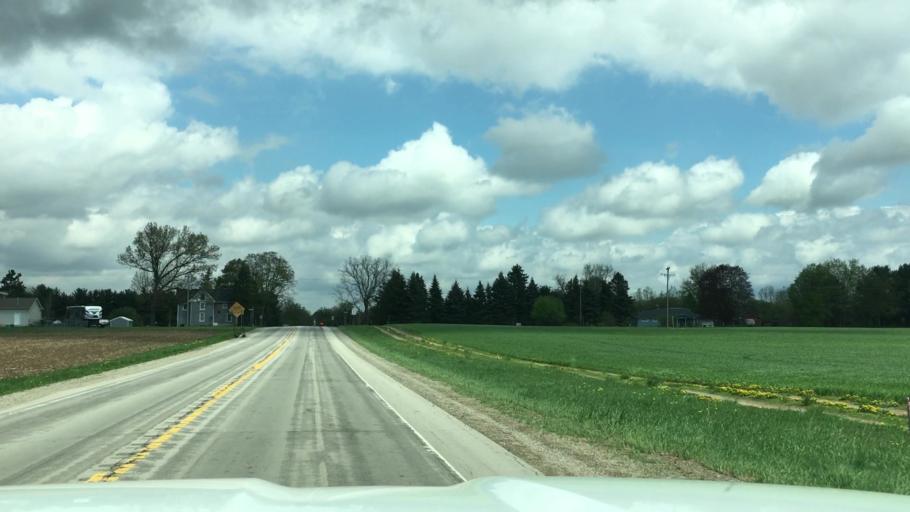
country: US
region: Michigan
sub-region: Ingham County
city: Stockbridge
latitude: 42.4668
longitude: -84.1901
